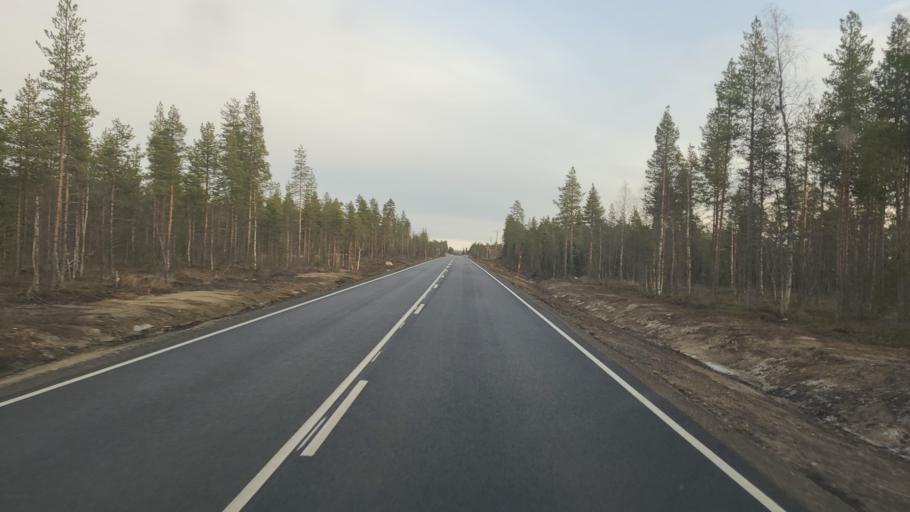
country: FI
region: Lapland
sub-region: Tunturi-Lappi
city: Kittilae
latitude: 67.8715
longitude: 24.9040
